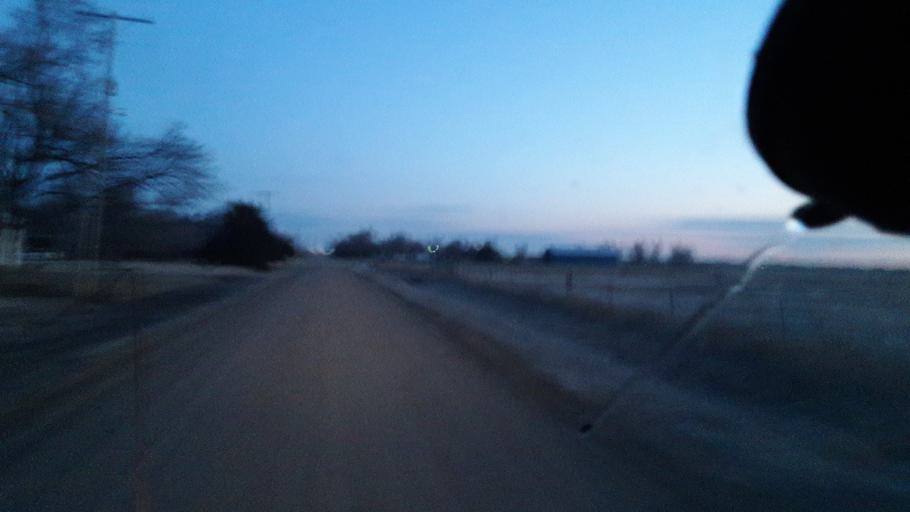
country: US
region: Kansas
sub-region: Reno County
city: South Hutchinson
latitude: 38.0014
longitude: -97.9771
